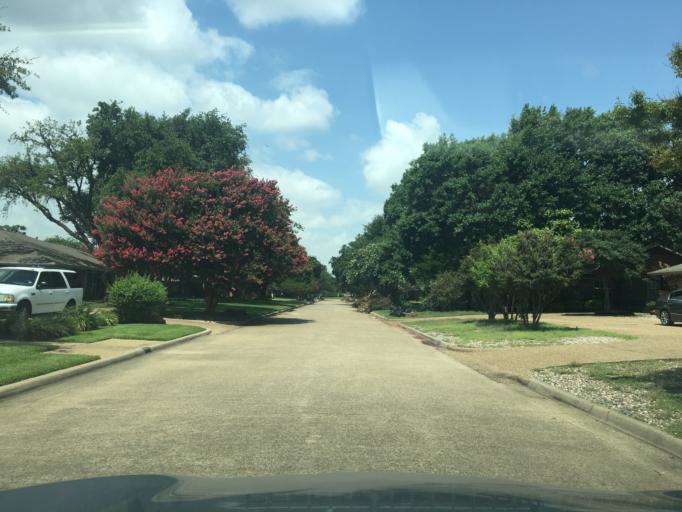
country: US
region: Texas
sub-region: Dallas County
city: Addison
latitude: 32.9232
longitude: -96.8311
